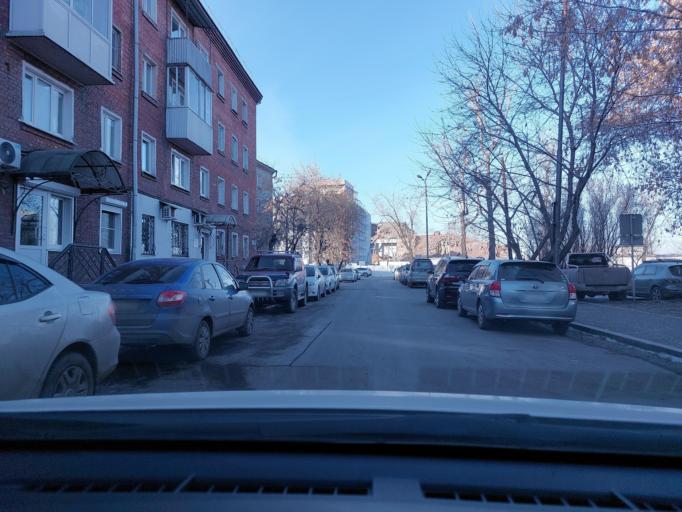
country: RU
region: Irkutsk
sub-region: Irkutskiy Rayon
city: Irkutsk
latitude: 52.2896
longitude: 104.2766
